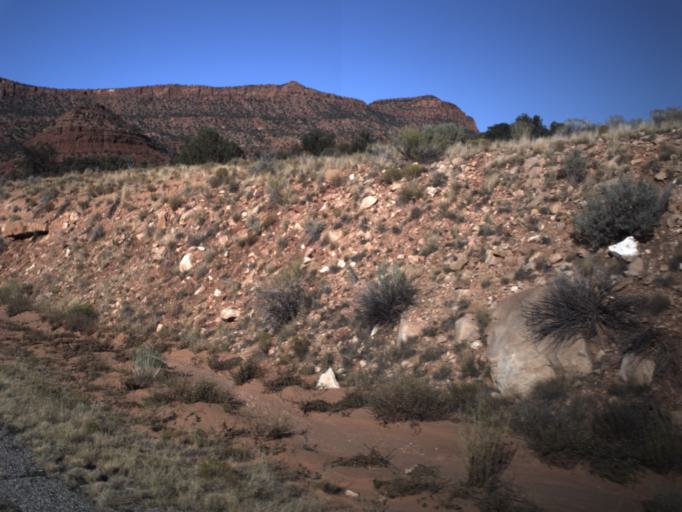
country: US
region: Utah
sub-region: San Juan County
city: Blanding
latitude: 37.6359
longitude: -110.1512
